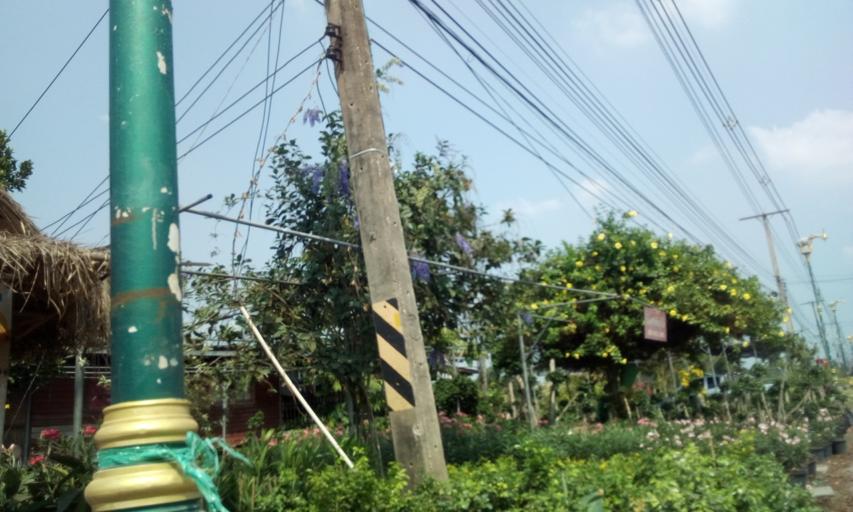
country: TH
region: Nakhon Nayok
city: Ongkharak
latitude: 14.1301
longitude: 100.9510
